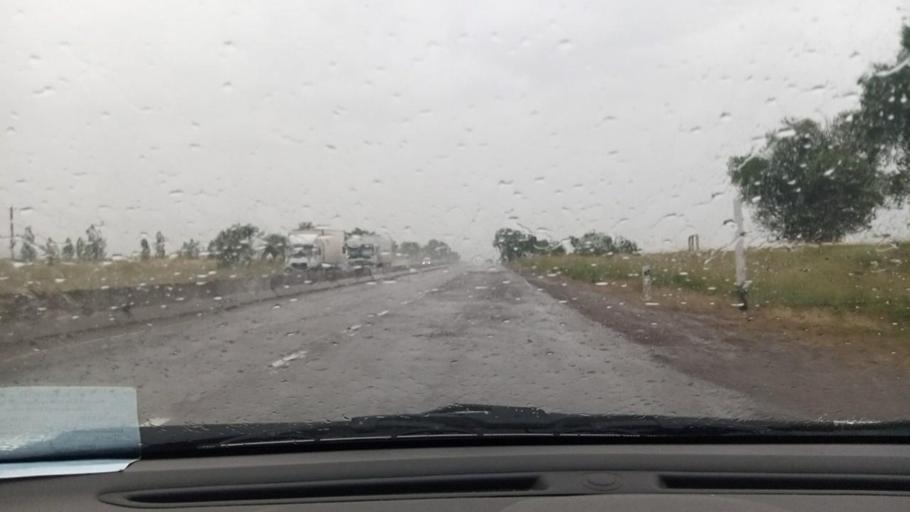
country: UZ
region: Toshkent
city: Angren
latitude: 40.9526
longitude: 69.9213
